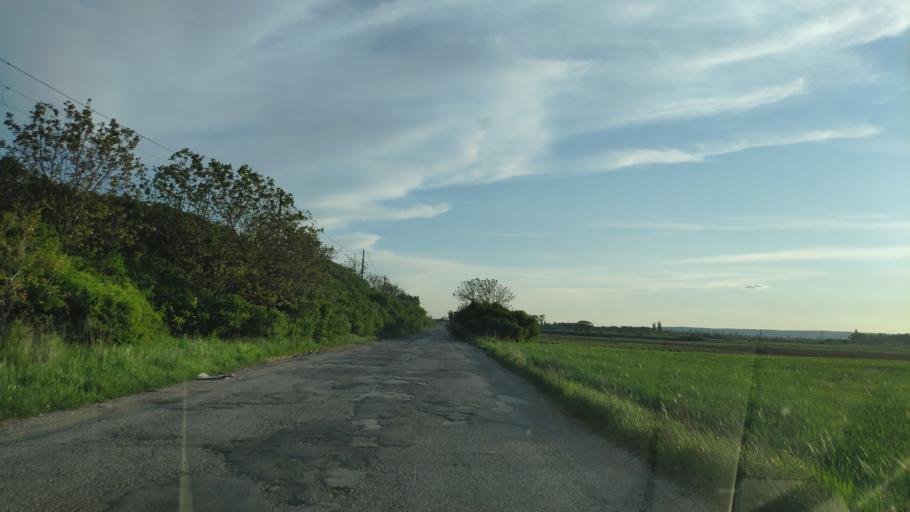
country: SK
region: Kosicky
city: Kosice
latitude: 48.6500
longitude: 21.2975
